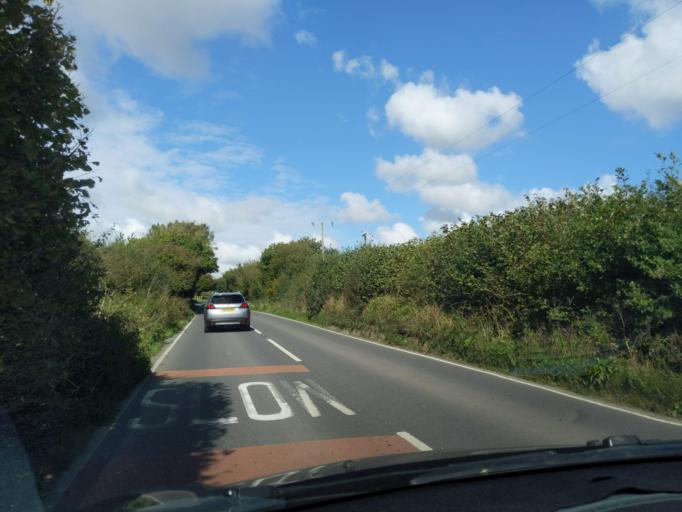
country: GB
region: England
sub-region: Devon
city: Holsworthy
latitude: 50.8253
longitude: -4.3438
